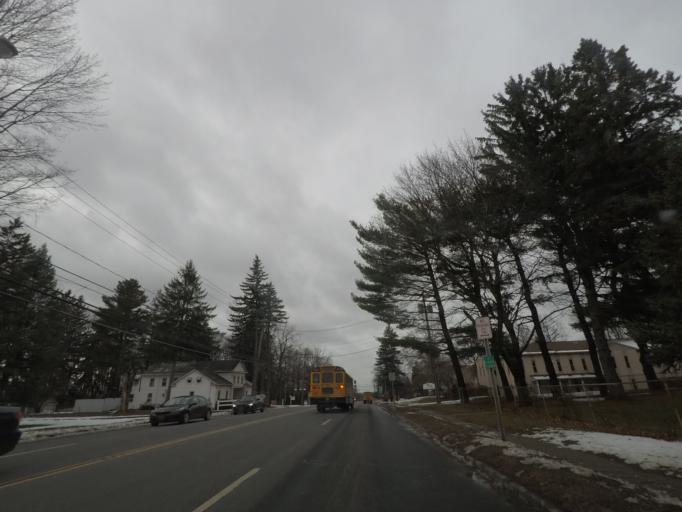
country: US
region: New York
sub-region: Rensselaer County
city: East Greenbush
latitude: 42.5894
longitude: -73.7001
